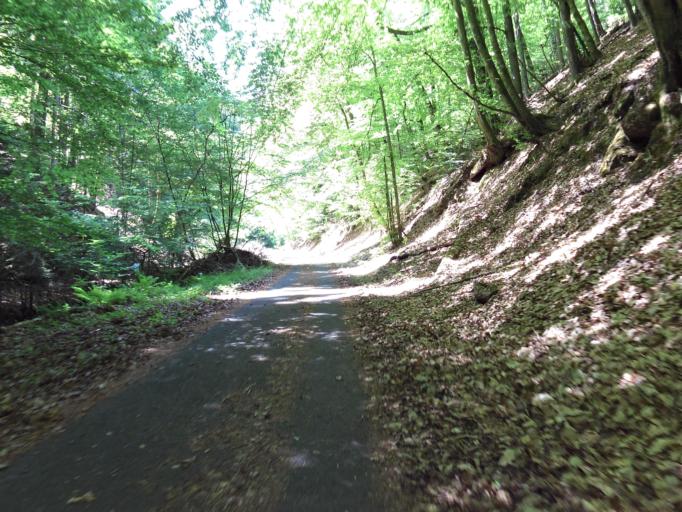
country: DE
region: Rheinland-Pfalz
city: Fischbach
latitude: 49.4235
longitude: 7.9437
